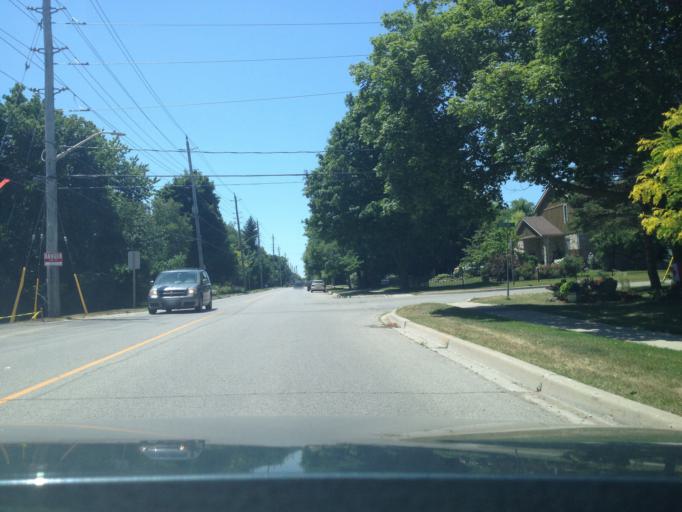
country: CA
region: Ontario
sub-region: Wellington County
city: Guelph
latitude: 43.6866
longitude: -80.4206
